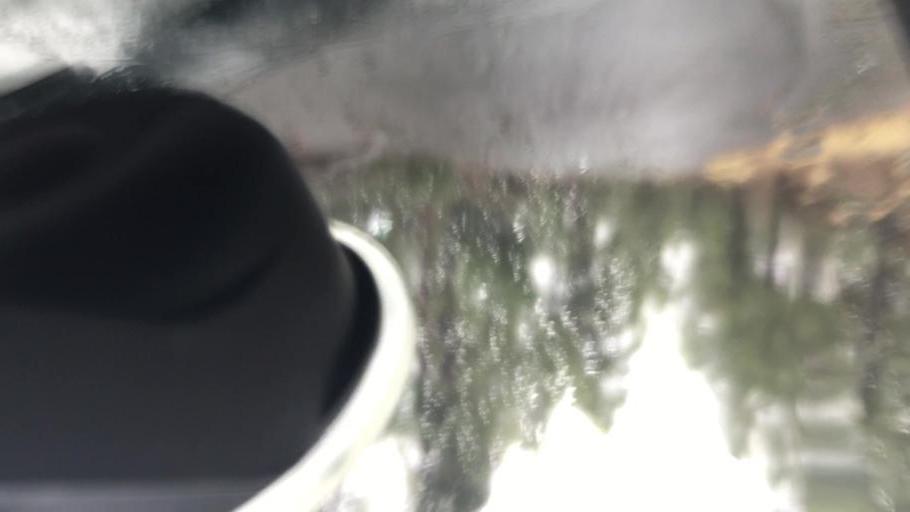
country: US
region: Arizona
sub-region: Yavapai County
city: Prescott
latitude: 34.5103
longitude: -112.3828
